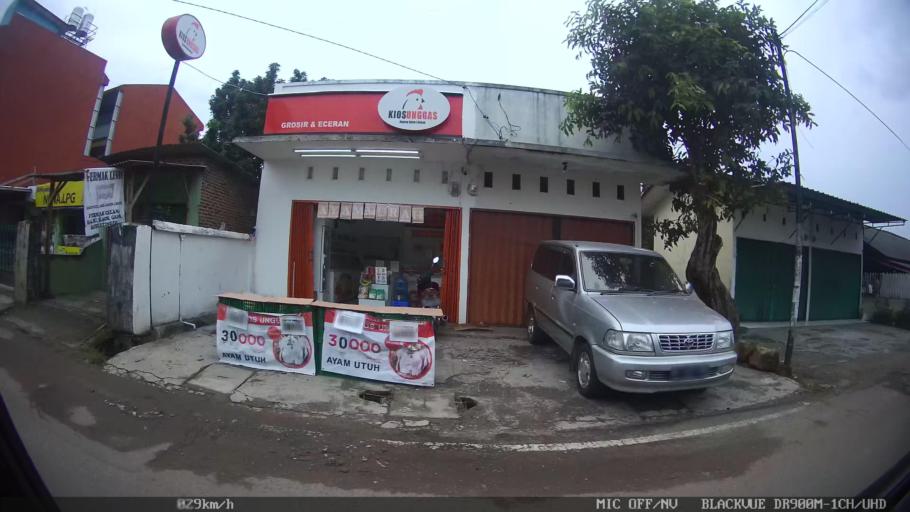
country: ID
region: Lampung
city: Kedaton
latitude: -5.3811
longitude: 105.2513
